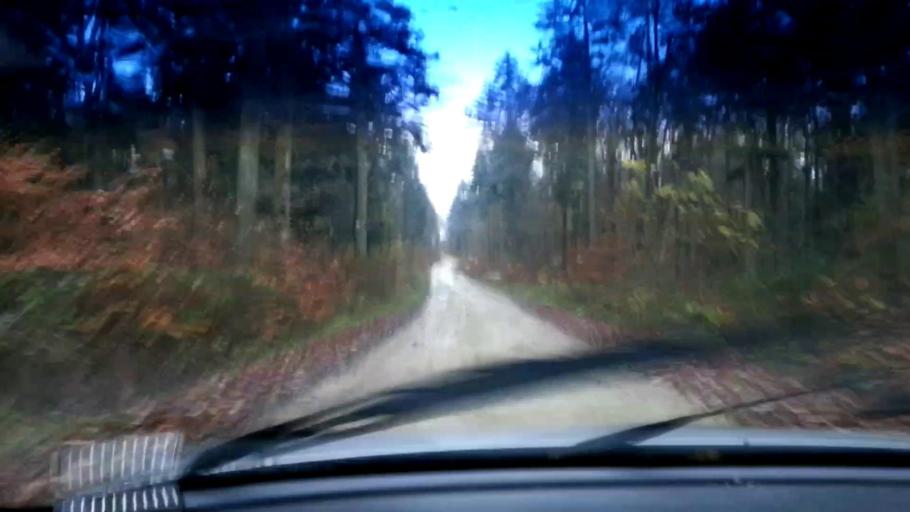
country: DE
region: Bavaria
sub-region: Upper Franconia
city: Schesslitz
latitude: 49.9581
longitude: 11.0327
